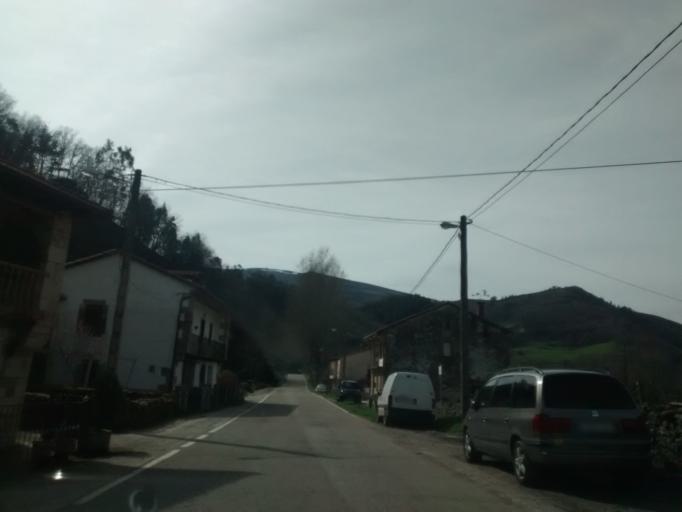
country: ES
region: Cantabria
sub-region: Provincia de Cantabria
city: Santiurde de Toranzo
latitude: 43.1682
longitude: -3.8907
